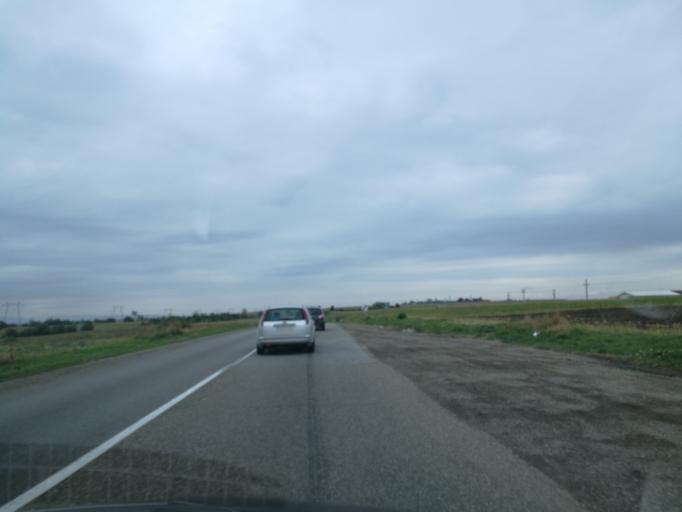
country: RO
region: Suceava
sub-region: Comuna Fantana Mare
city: Fantana Mare
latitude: 47.4086
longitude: 26.3201
